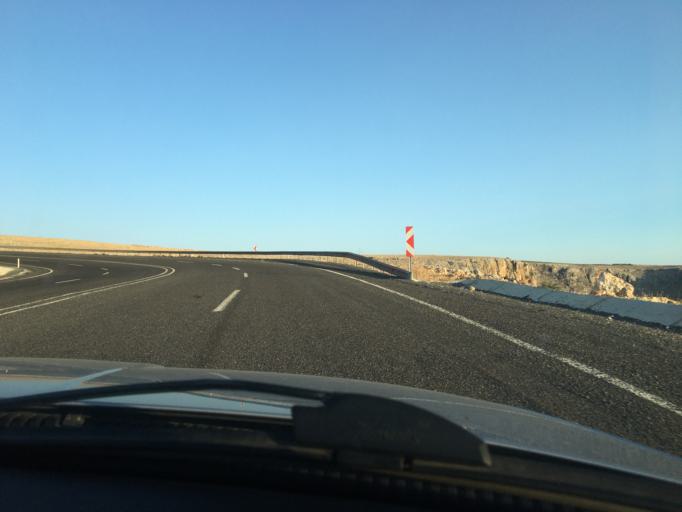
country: TR
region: Sanliurfa
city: Halfeti
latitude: 37.2386
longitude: 37.8832
